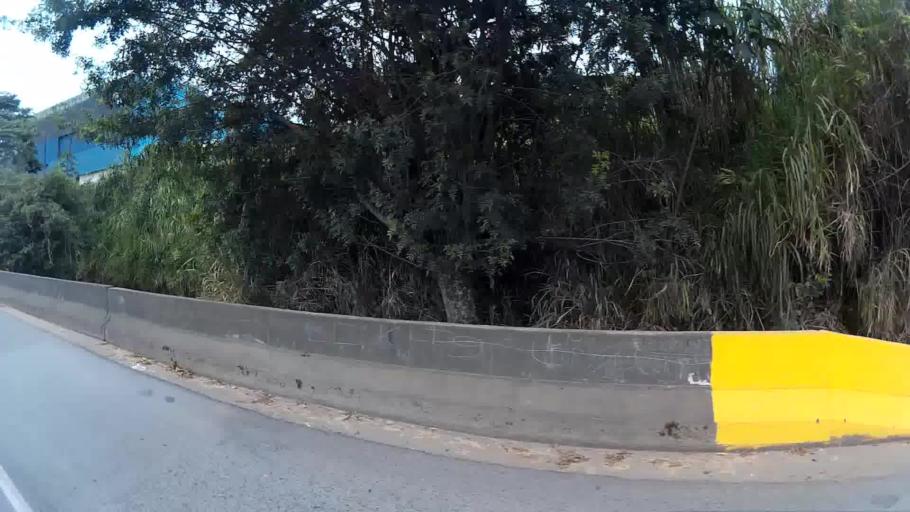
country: CO
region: Risaralda
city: Pereira
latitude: 4.8145
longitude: -75.7617
